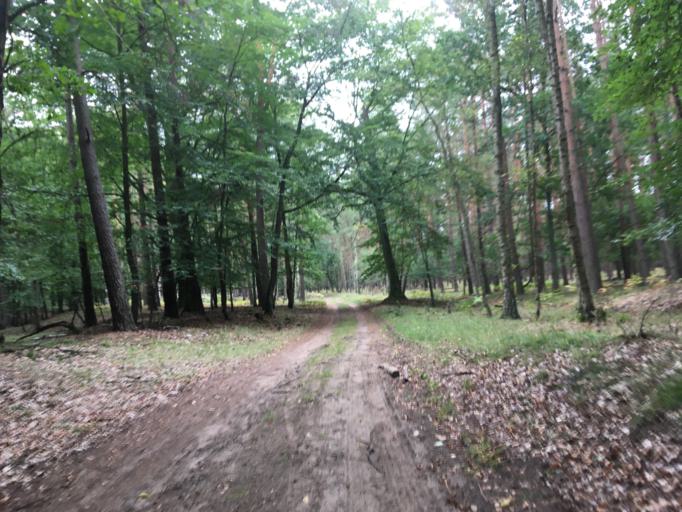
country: DE
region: Brandenburg
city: Zehdenick
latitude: 53.0391
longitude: 13.3381
